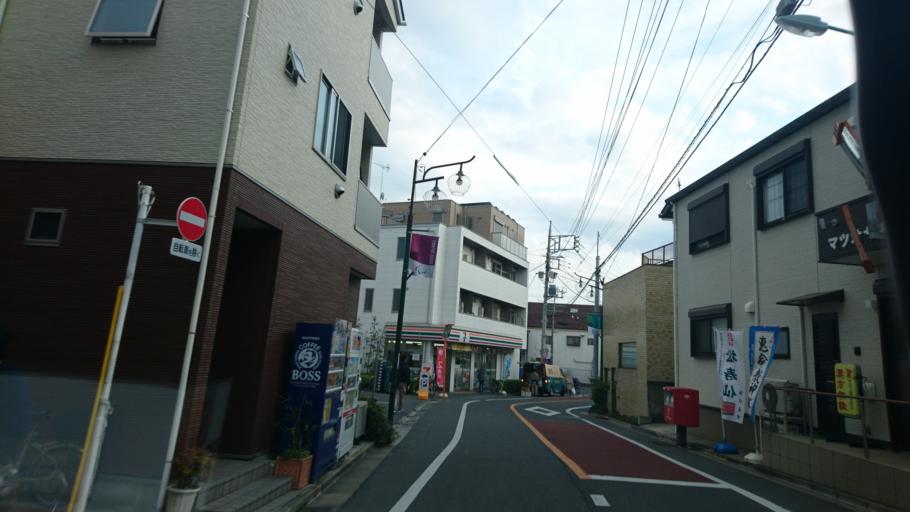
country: JP
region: Kanagawa
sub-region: Kawasaki-shi
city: Kawasaki
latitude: 35.5980
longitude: 139.7230
